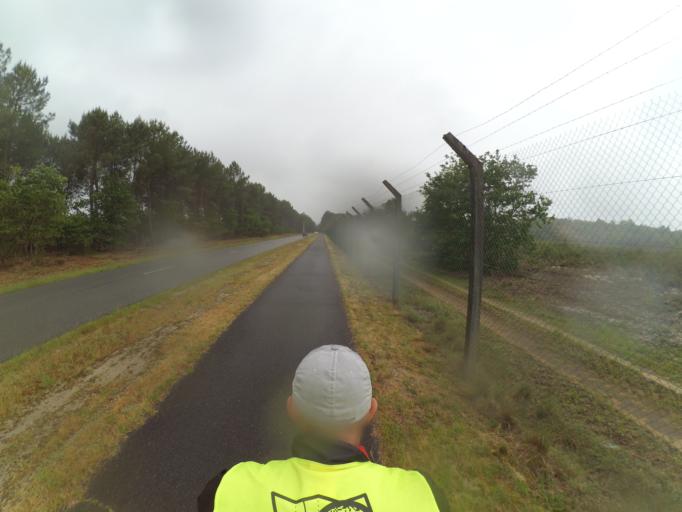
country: FR
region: Aquitaine
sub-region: Departement des Landes
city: Mimizan
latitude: 44.2403
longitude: -1.2066
